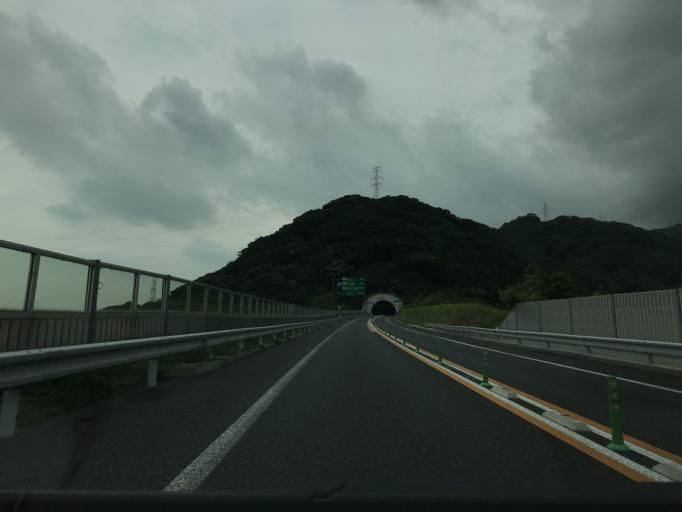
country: JP
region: Fukuoka
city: Kanda
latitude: 33.7796
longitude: 130.9712
